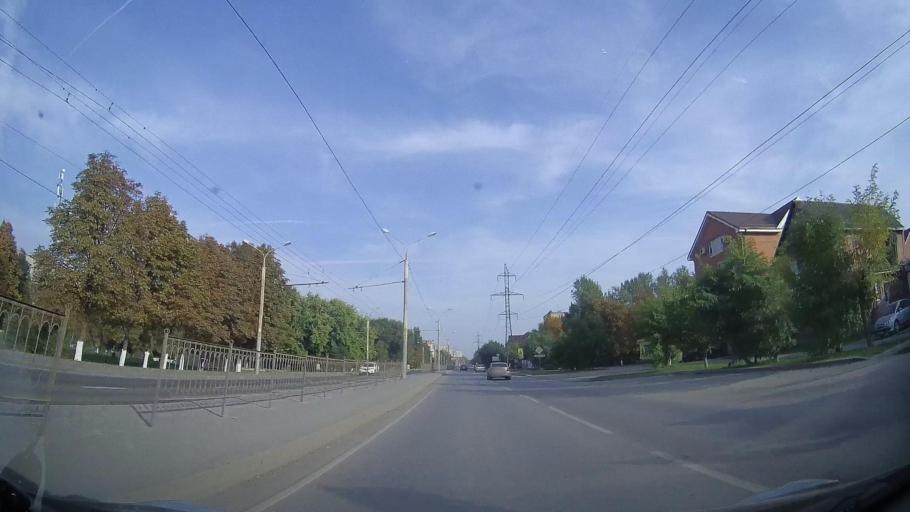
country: RU
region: Rostov
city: Imeni Chkalova
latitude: 47.2855
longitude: 39.7458
